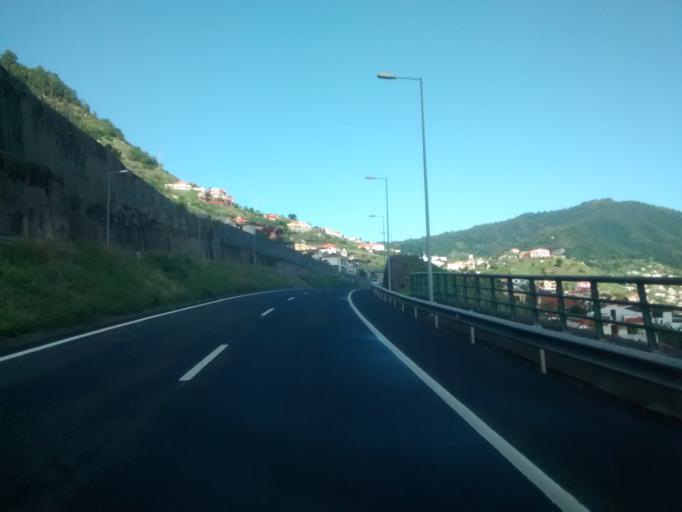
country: PT
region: Madeira
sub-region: Machico
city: Machico
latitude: 32.7197
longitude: -16.7733
